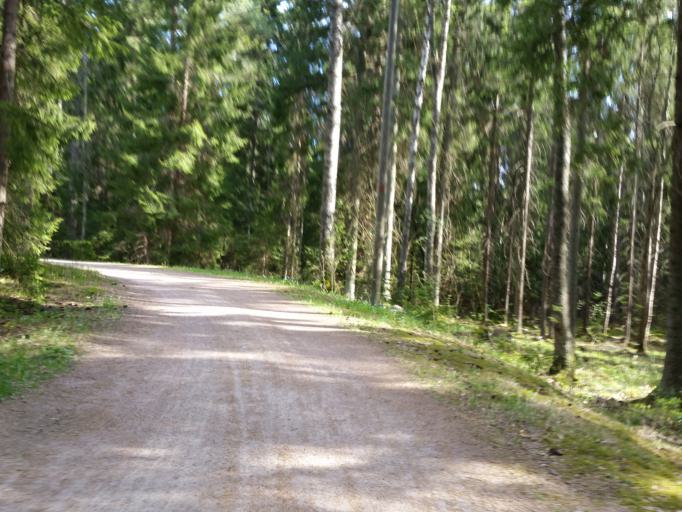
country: FI
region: Uusimaa
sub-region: Helsinki
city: Kauniainen
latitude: 60.1839
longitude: 24.7121
